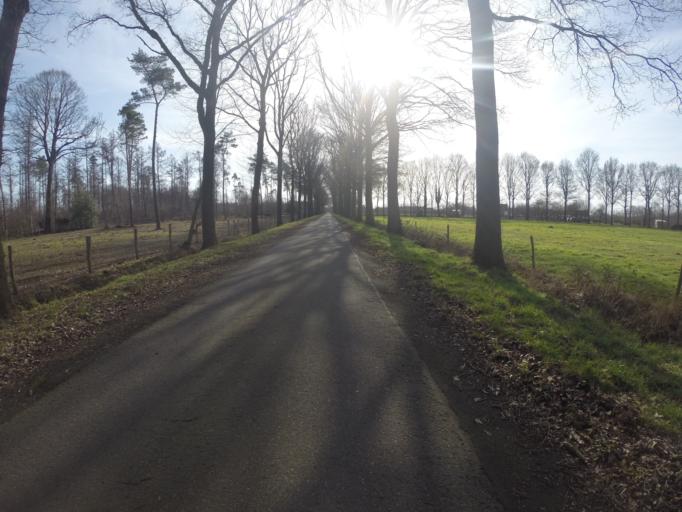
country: BE
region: Flanders
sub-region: Provincie West-Vlaanderen
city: Oostkamp
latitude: 51.1200
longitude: 3.2390
